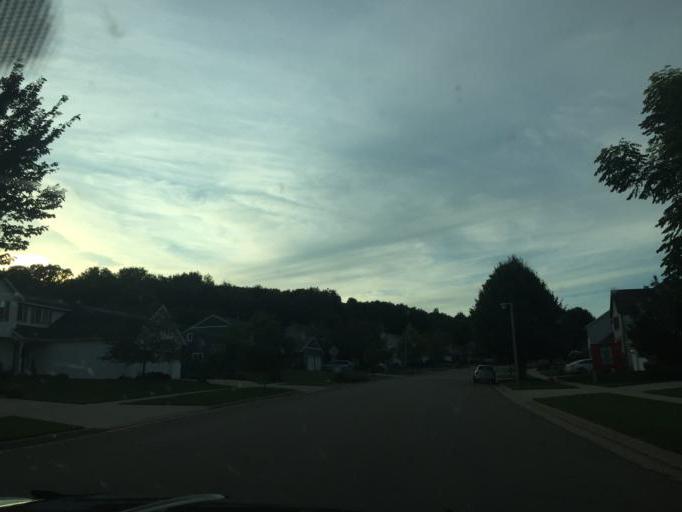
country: US
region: Minnesota
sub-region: Olmsted County
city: Rochester
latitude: 44.0060
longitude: -92.4901
